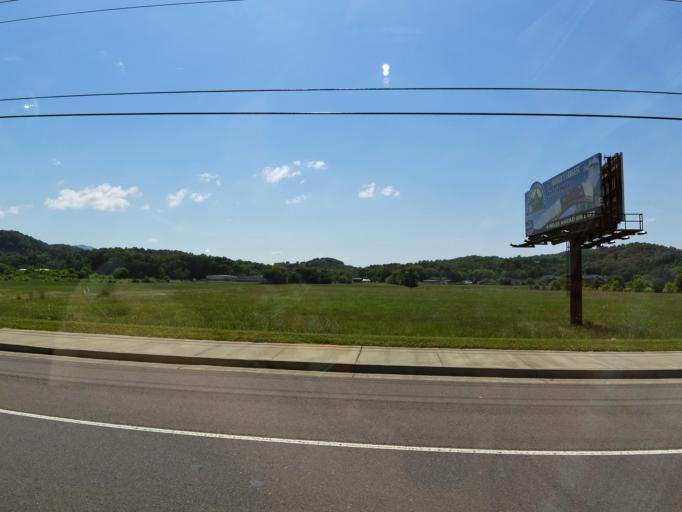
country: US
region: Tennessee
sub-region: Sevier County
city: Sevierville
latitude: 35.8834
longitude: -83.5730
